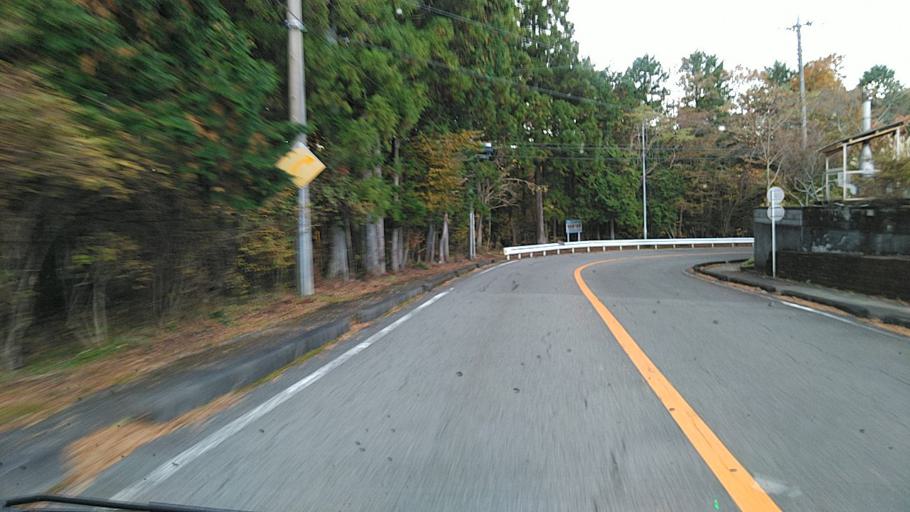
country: JP
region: Shizuoka
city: Gotemba
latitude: 35.3595
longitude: 138.8706
